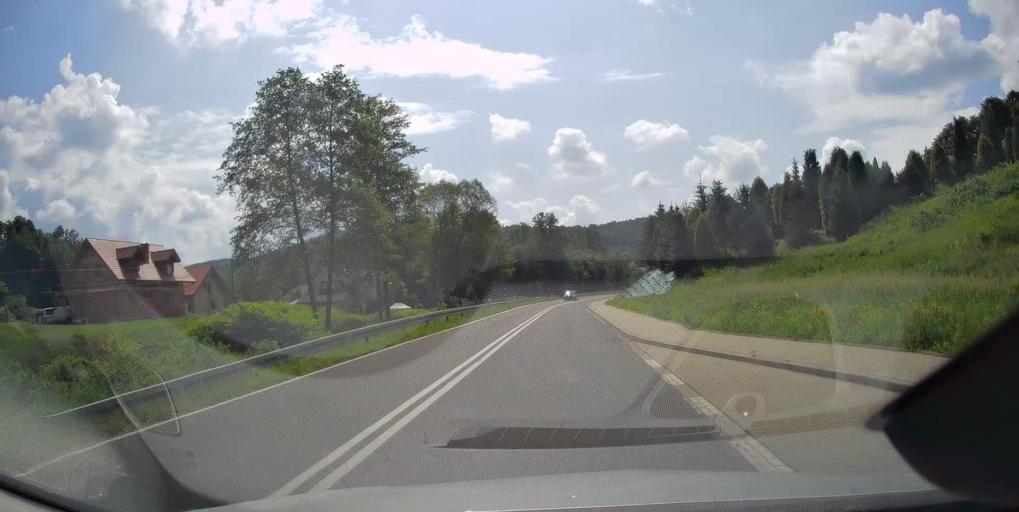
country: PL
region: Lesser Poland Voivodeship
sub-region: Powiat tarnowski
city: Zakliczyn
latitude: 49.7972
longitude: 20.7988
